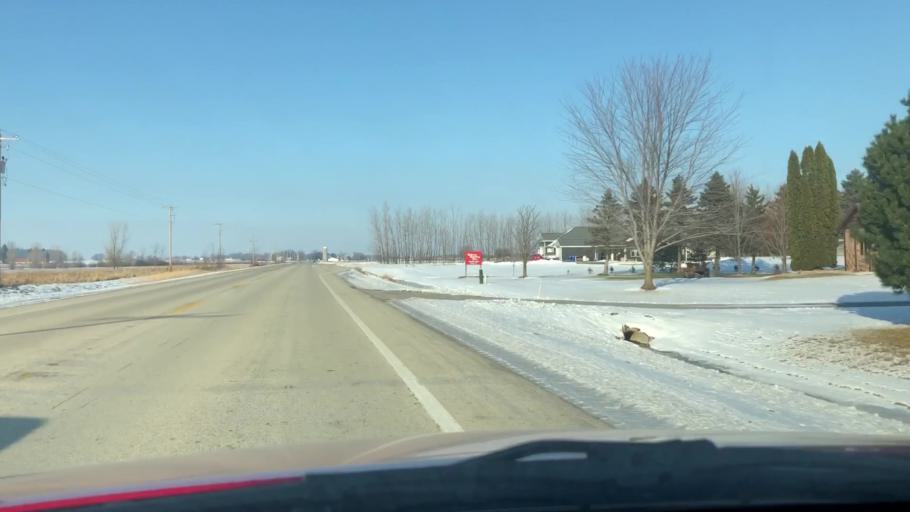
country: US
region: Wisconsin
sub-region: Outagamie County
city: Seymour
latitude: 44.4787
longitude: -88.3295
